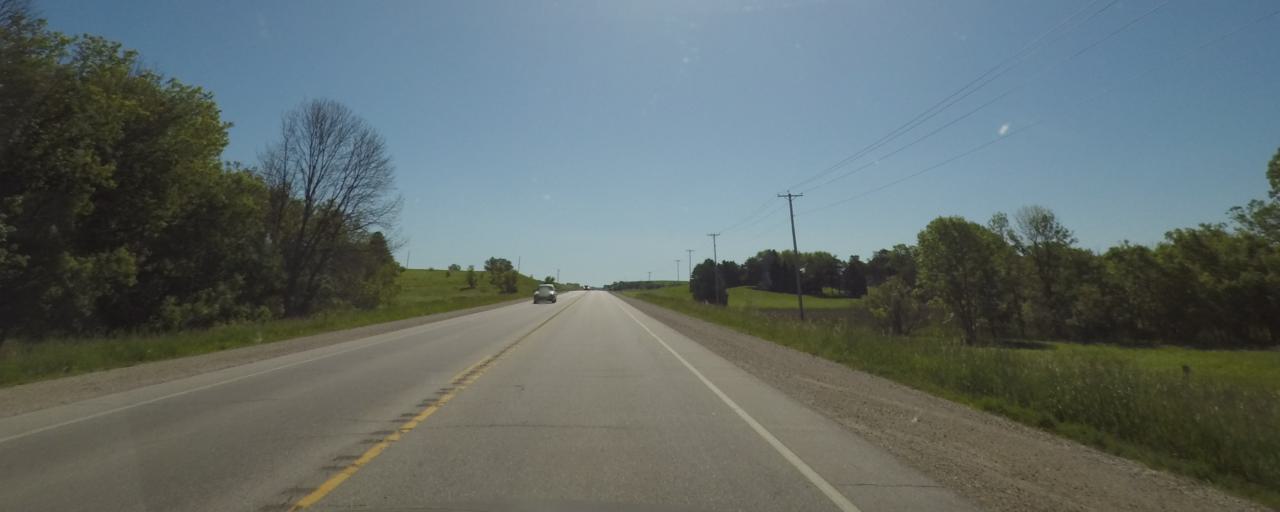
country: US
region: Wisconsin
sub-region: Fond du Lac County
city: Saint Peter
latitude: 43.7834
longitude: -88.3330
